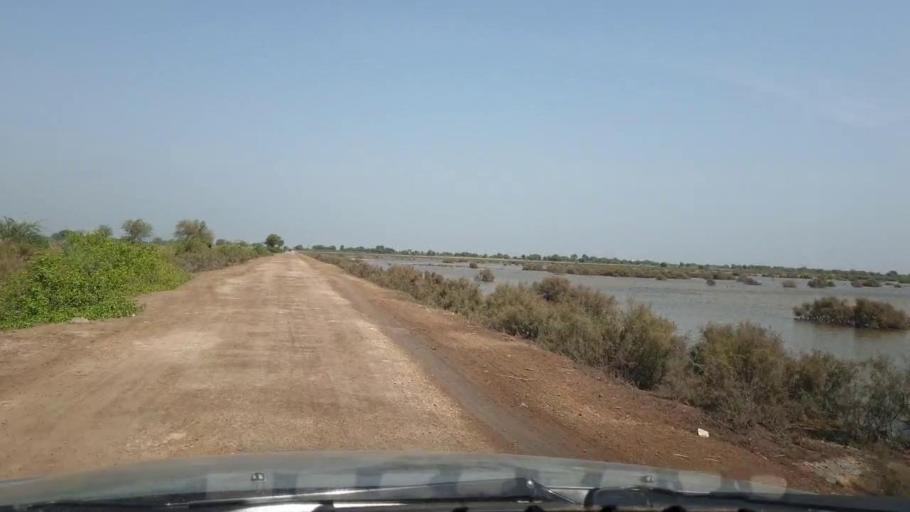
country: PK
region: Sindh
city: Tando Muhammad Khan
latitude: 25.1396
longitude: 68.6315
